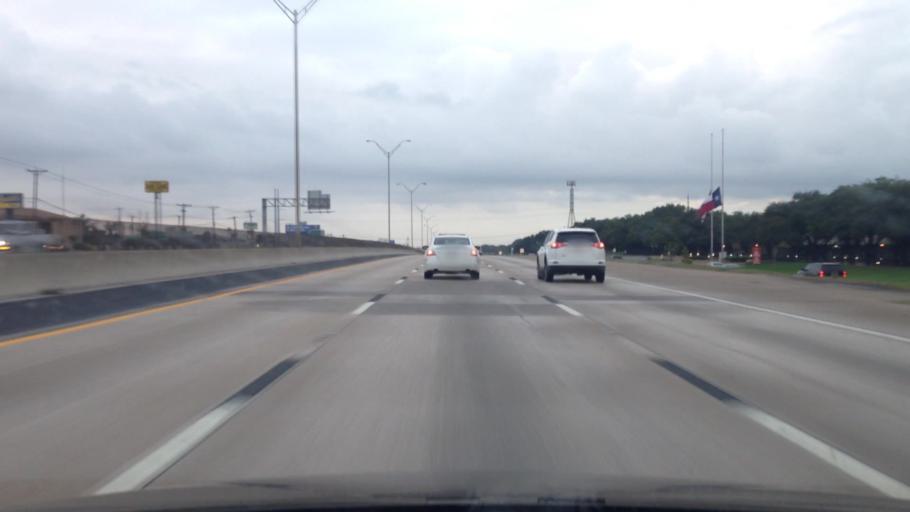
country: US
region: Texas
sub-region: Tarrant County
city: Edgecliff Village
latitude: 32.6415
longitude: -97.3214
